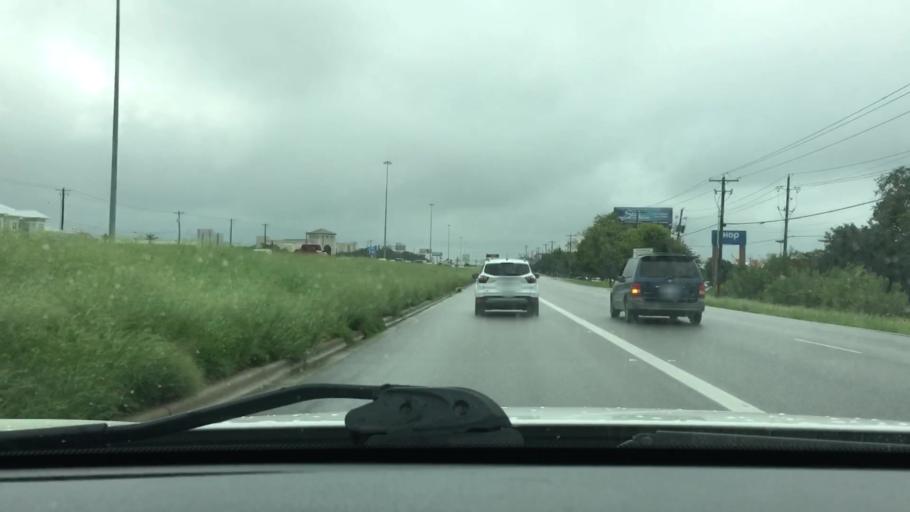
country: US
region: Texas
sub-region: Travis County
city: Wells Branch
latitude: 30.4349
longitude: -97.6698
